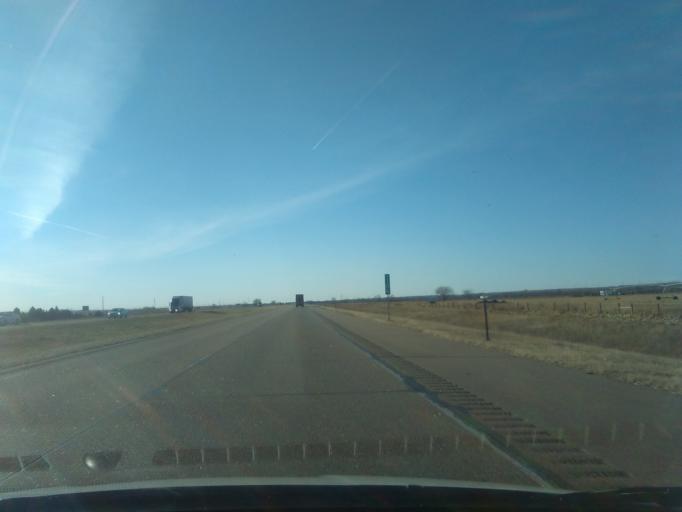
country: US
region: Colorado
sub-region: Sedgwick County
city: Julesburg
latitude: 41.0423
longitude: -102.0955
